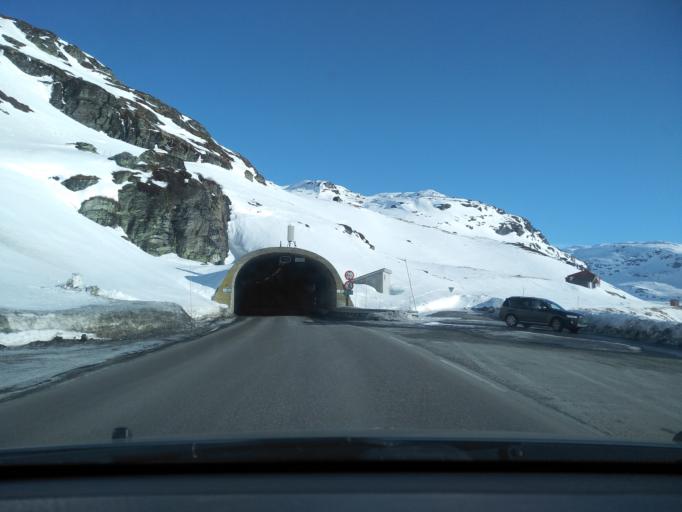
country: NO
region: Aust-Agder
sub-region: Bykle
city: Hovden
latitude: 59.8394
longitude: 6.9882
